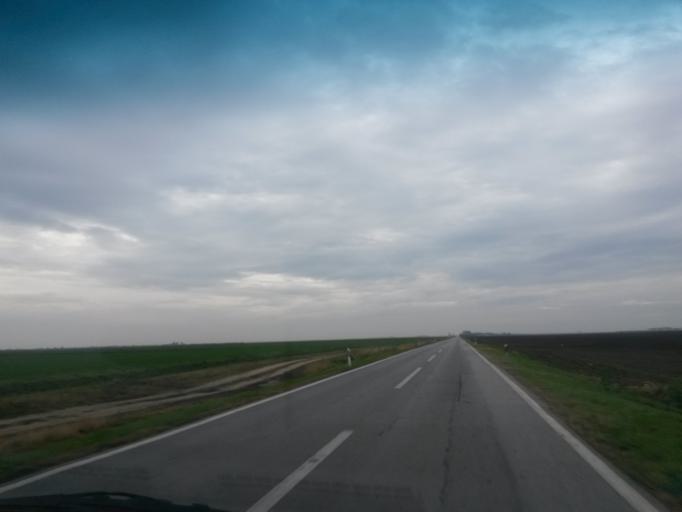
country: HR
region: Vukovarsko-Srijemska
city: Bobota
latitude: 45.4637
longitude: 18.8483
